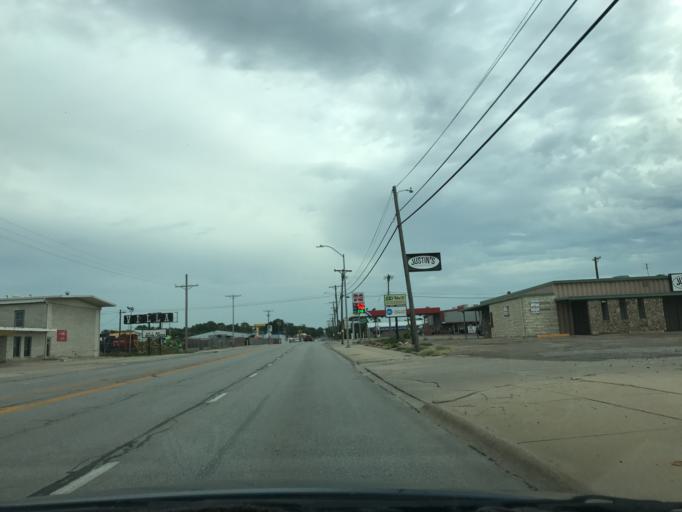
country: US
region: Nebraska
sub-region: Gage County
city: Beatrice
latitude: 40.2839
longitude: -96.7467
